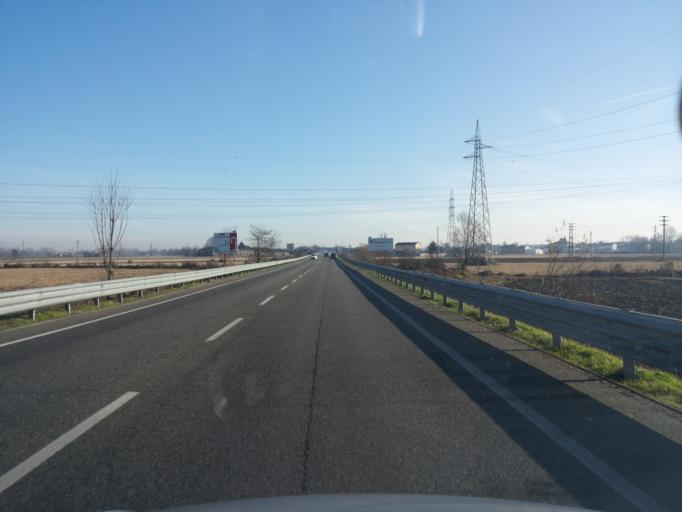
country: IT
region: Piedmont
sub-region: Provincia di Vercelli
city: Vercelli
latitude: 45.3415
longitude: 8.4091
